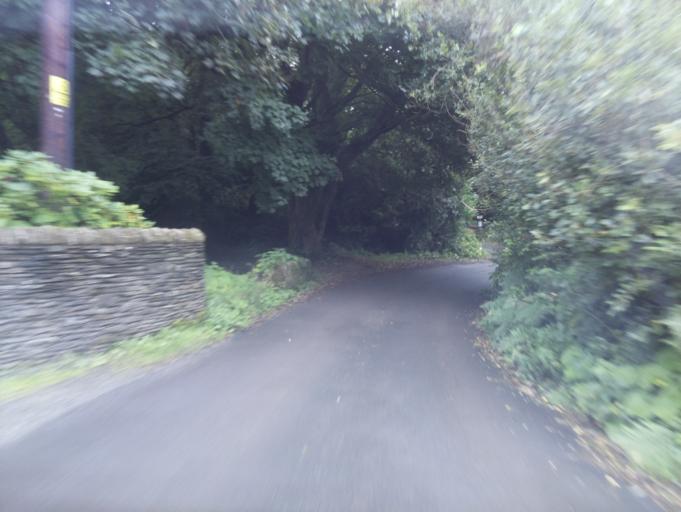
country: GB
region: England
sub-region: Devon
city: Kingsbridge
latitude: 50.3216
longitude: -3.7140
